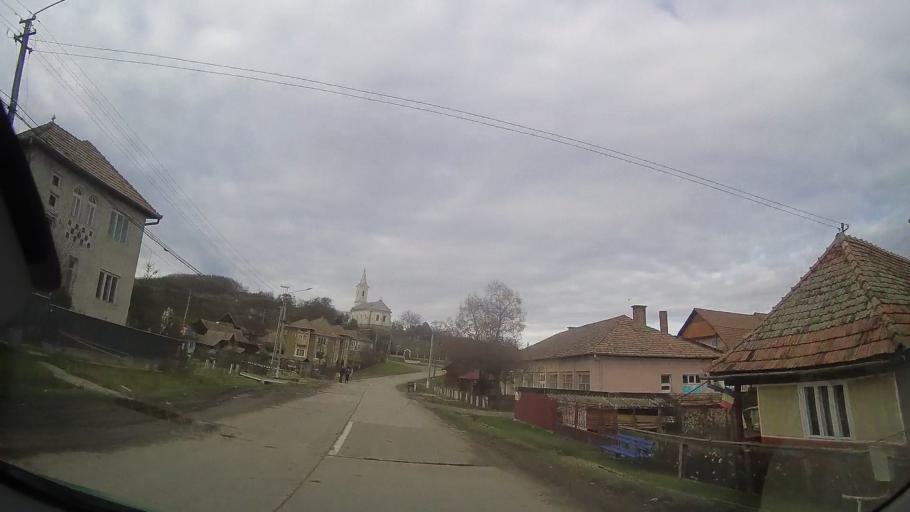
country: RO
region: Bistrita-Nasaud
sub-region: Comuna Micestii de Campie
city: Micestii de Campie
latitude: 46.8594
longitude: 24.3109
